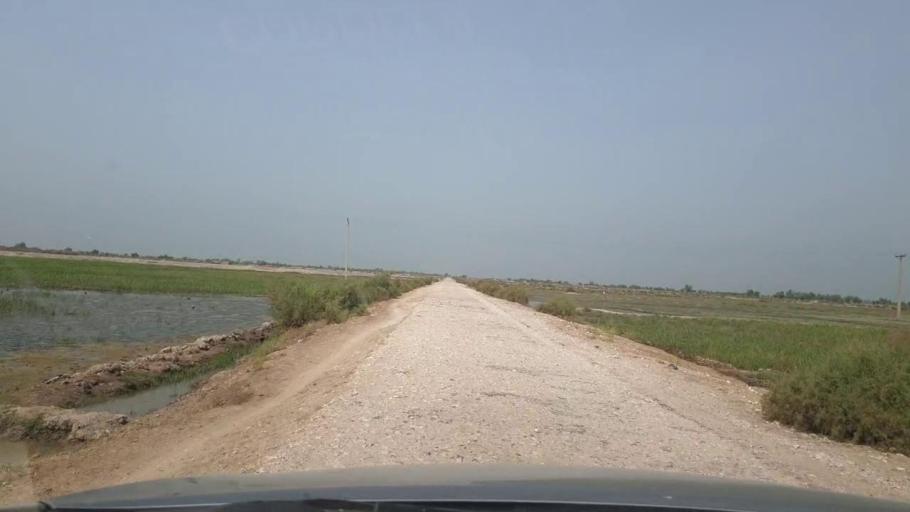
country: PK
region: Sindh
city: Garhi Yasin
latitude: 27.9150
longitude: 68.4202
